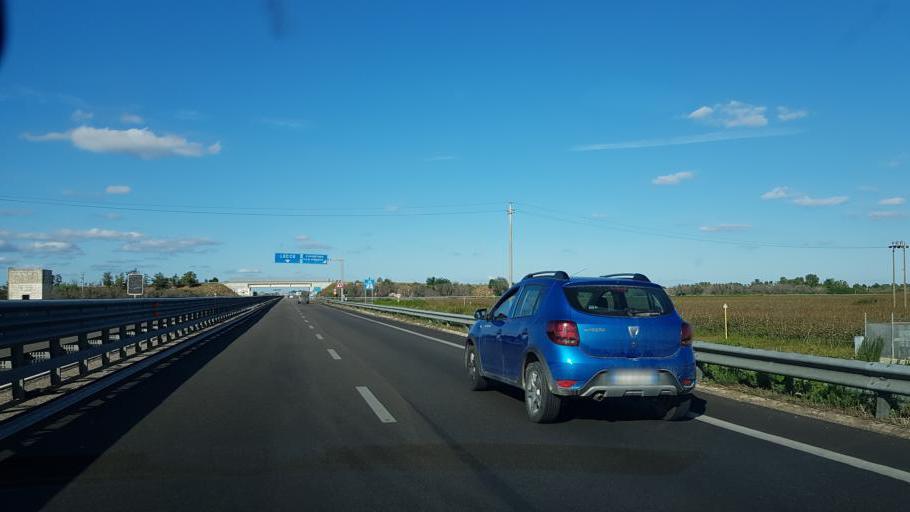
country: IT
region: Apulia
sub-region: Provincia di Lecce
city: Collemeto
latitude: 40.2547
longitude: 18.1174
